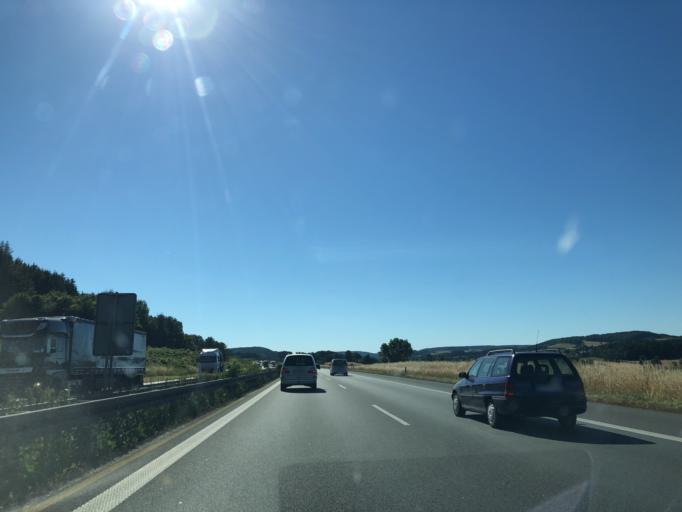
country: DE
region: Bavaria
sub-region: Regierungsbezirk Mittelfranken
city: Burghaslach
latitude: 49.7628
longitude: 10.5469
